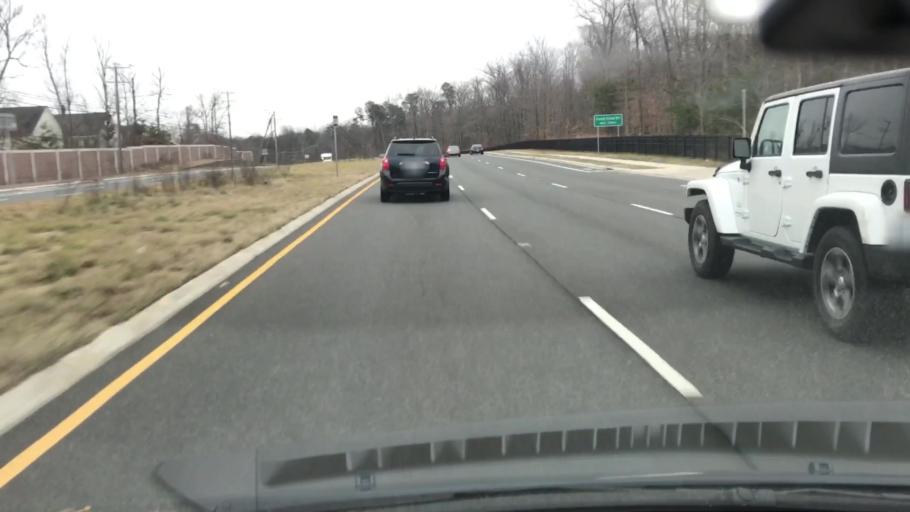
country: US
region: Virginia
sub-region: Fairfax County
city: Newington
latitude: 38.7079
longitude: -77.1878
